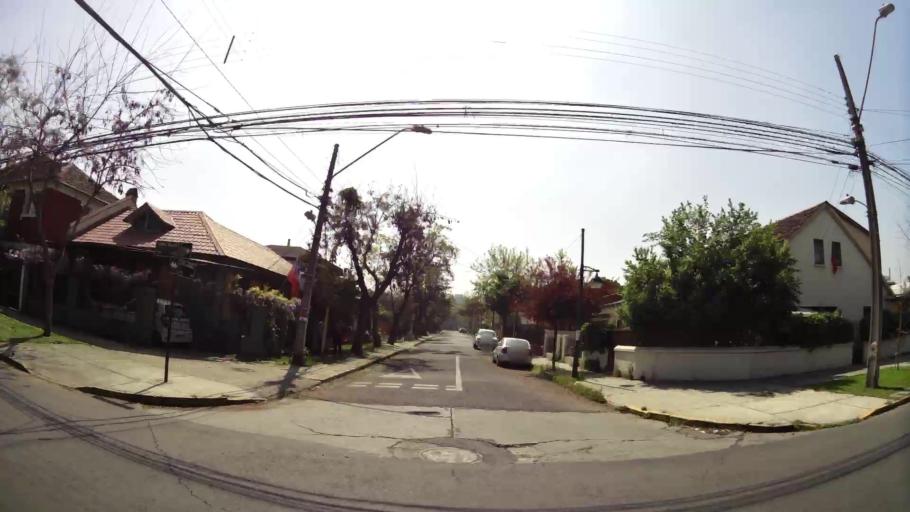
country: CL
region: Santiago Metropolitan
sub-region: Provincia de Santiago
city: Santiago
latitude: -33.4594
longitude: -70.6178
